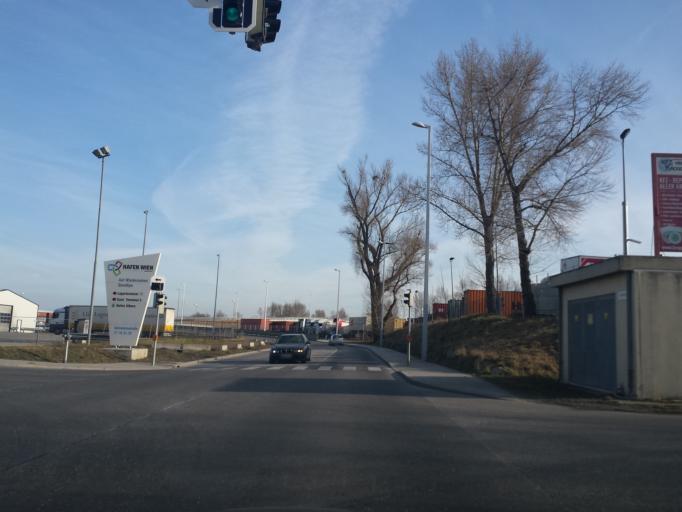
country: AT
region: Lower Austria
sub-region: Politischer Bezirk Wien-Umgebung
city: Schwechat
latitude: 48.1793
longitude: 16.4615
